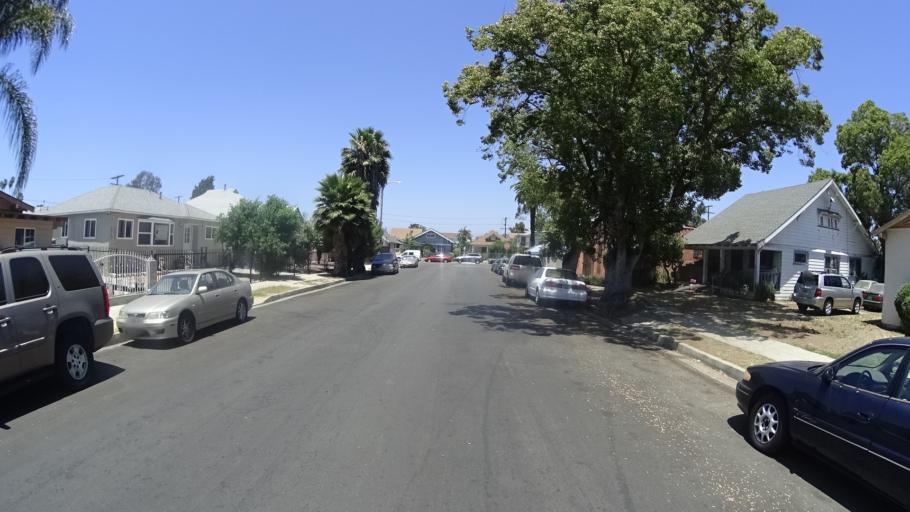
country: US
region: California
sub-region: Los Angeles County
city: View Park-Windsor Hills
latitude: 34.0149
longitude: -118.3010
